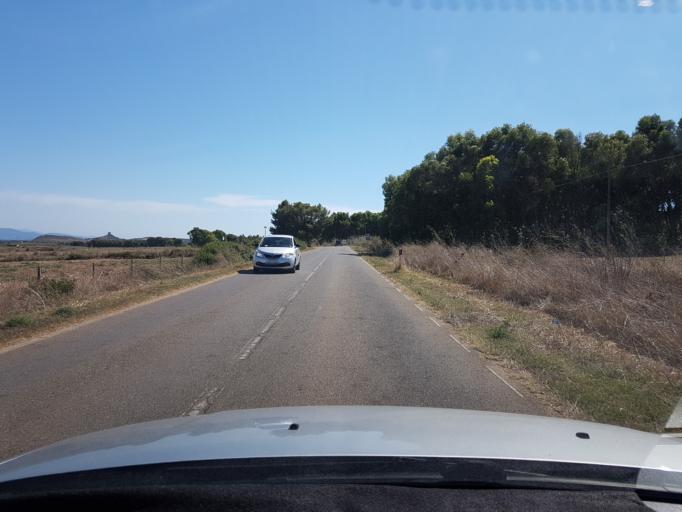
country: IT
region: Sardinia
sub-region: Provincia di Oristano
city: Cabras
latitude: 39.8995
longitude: 8.4350
